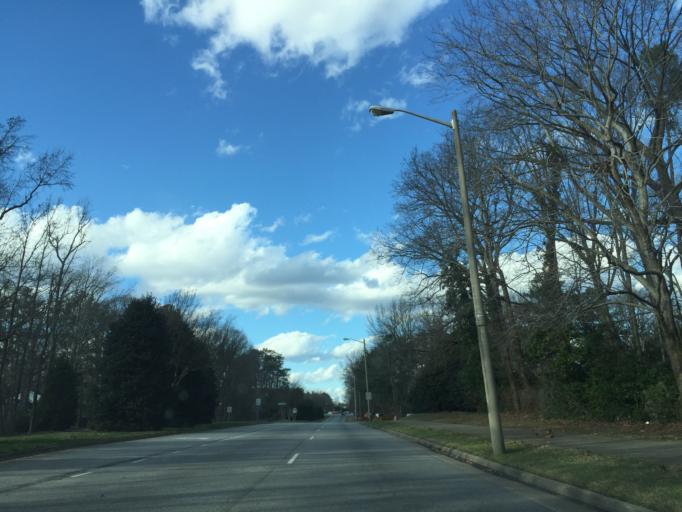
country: US
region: Virginia
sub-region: York County
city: Yorktown
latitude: 37.1007
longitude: -76.5097
